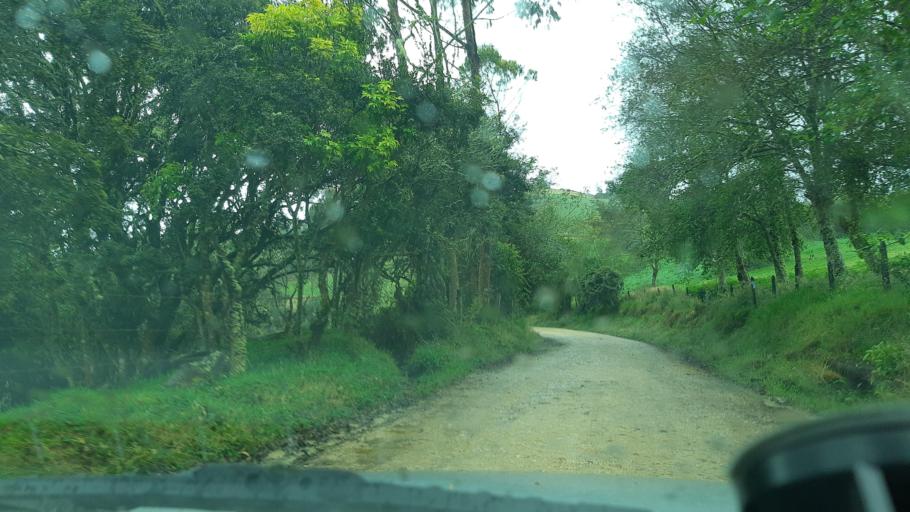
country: CO
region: Cundinamarca
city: Villapinzon
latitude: 5.2083
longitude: -73.5623
